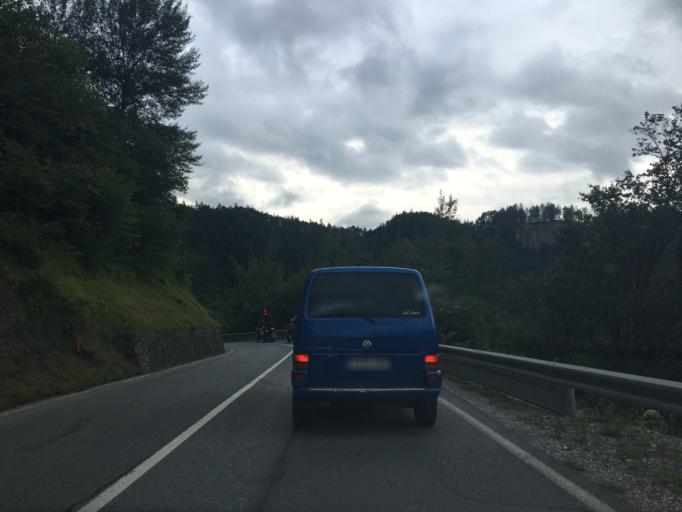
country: AT
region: Tyrol
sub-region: Politischer Bezirk Innsbruck Land
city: Patsch
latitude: 47.2005
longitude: 11.4015
